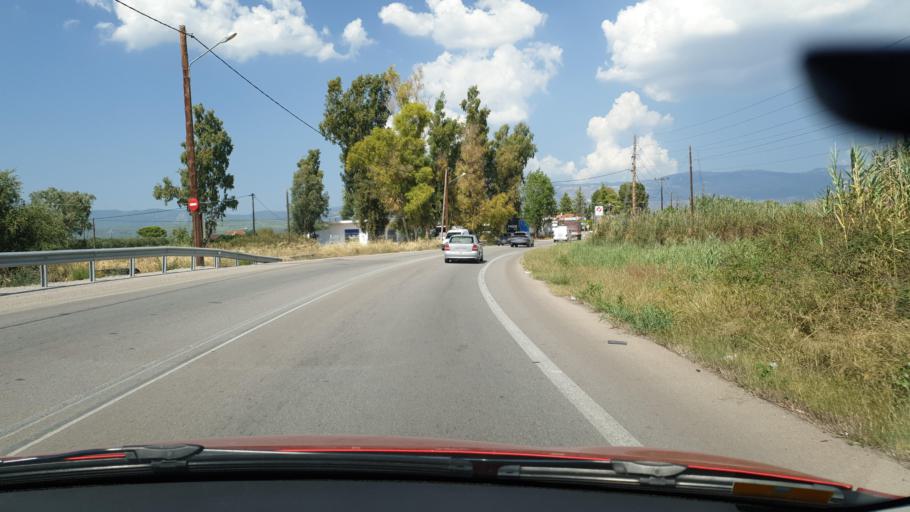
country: GR
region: Central Greece
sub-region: Nomos Evvoias
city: Kastella
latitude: 38.5430
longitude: 23.6270
